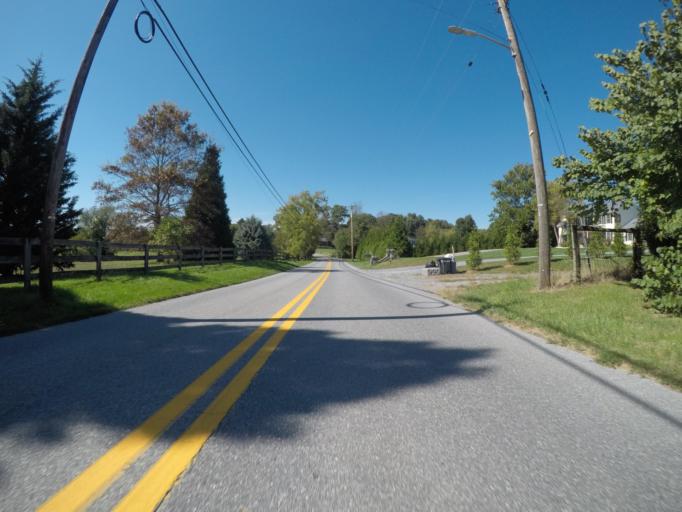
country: US
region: Maryland
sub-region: Carroll County
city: Hampstead
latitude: 39.5441
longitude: -76.7980
